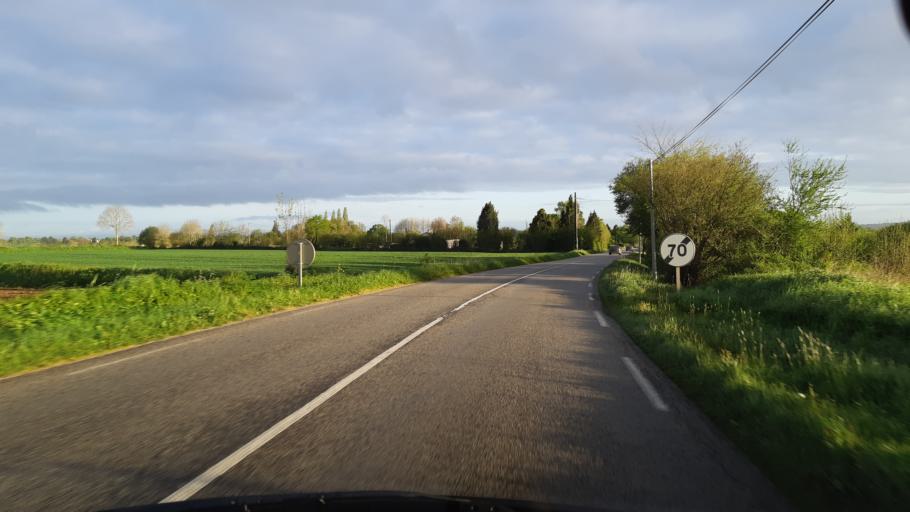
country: FR
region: Lower Normandy
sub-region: Departement de la Manche
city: Agneaux
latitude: 49.0548
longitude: -1.1321
